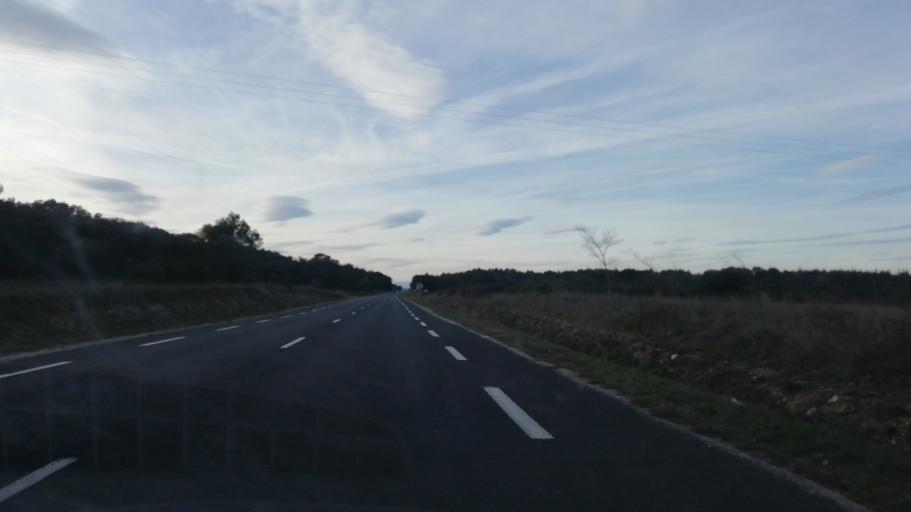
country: FR
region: Languedoc-Roussillon
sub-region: Departement du Gard
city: Caveirac
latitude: 43.8531
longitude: 4.2663
